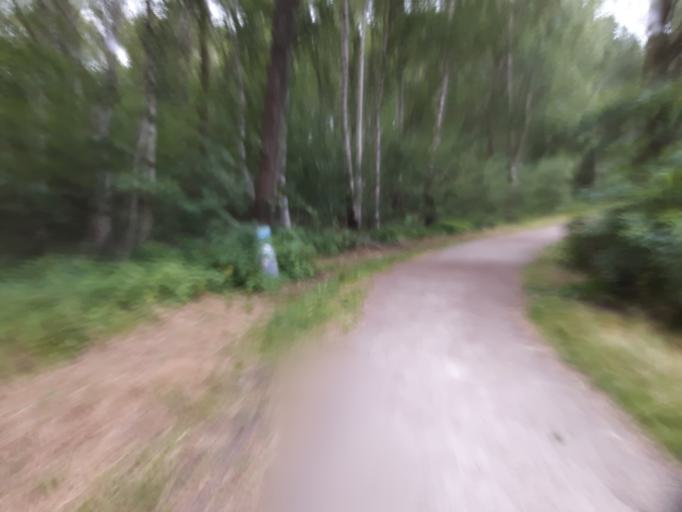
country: DE
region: Lower Saxony
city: Stelle
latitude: 53.4206
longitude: 10.0524
